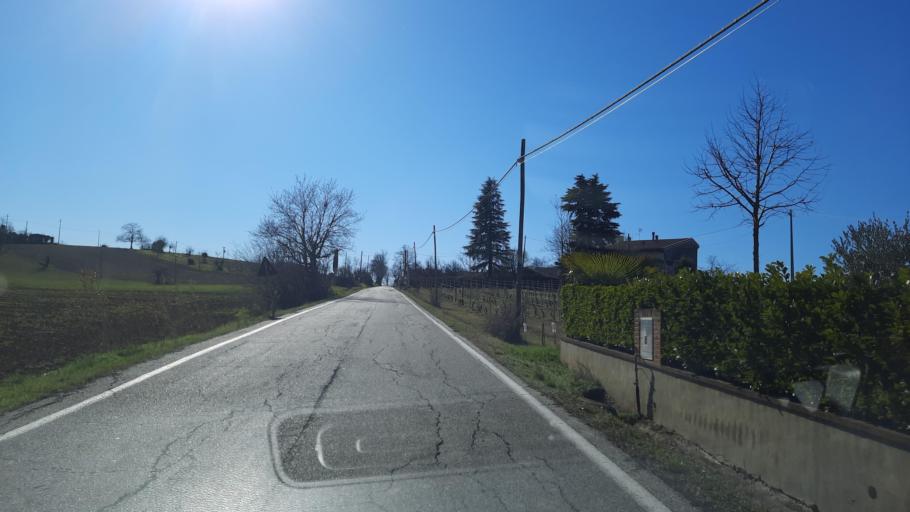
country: IT
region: Piedmont
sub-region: Provincia di Alessandria
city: Olivola
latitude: 45.0388
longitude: 8.3753
